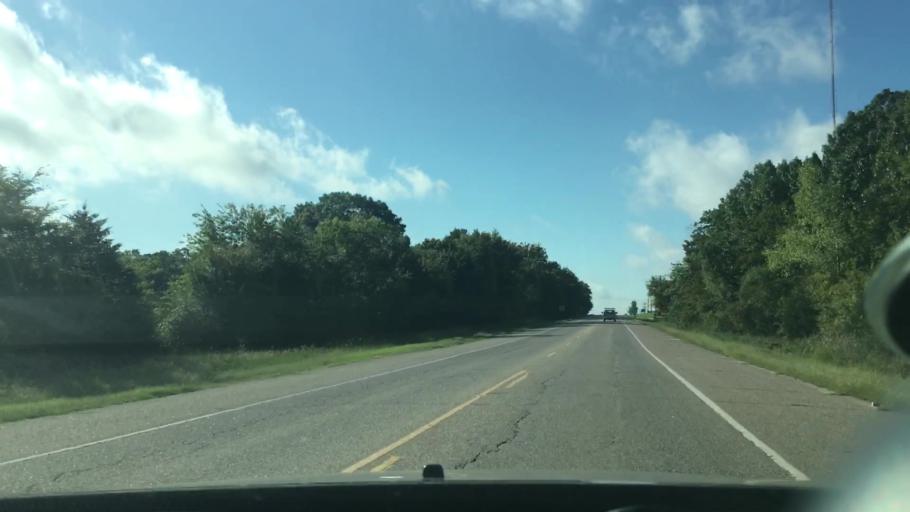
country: US
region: Oklahoma
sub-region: Bryan County
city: Durant
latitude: 34.0305
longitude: -96.3730
